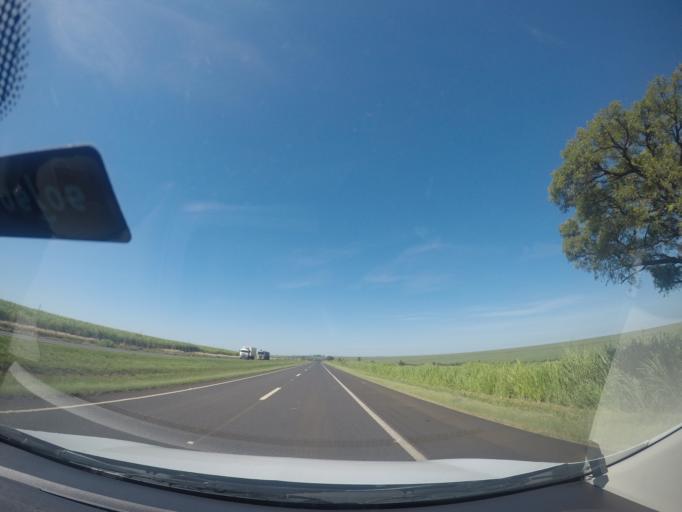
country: BR
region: Goias
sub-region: Morrinhos
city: Morrinhos
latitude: -17.8639
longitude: -49.2244
